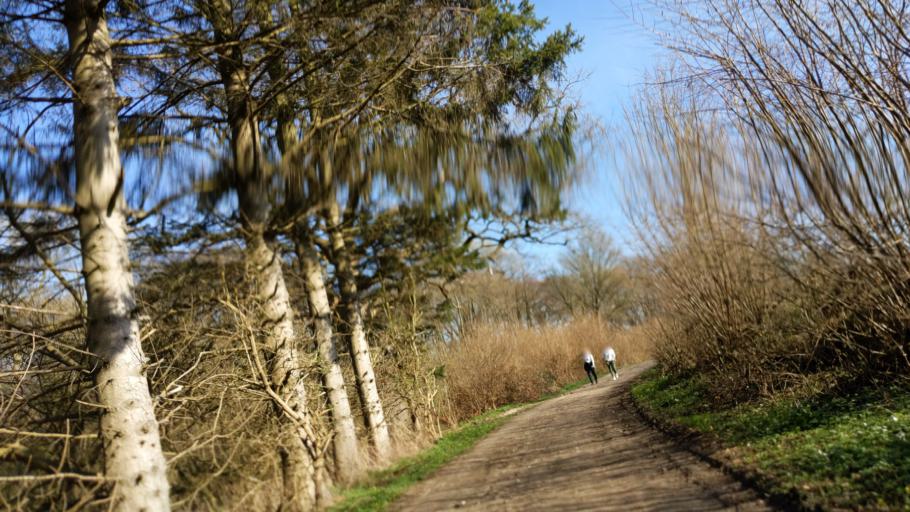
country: DE
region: Schleswig-Holstein
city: Travemuende
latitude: 53.9832
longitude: 10.8268
